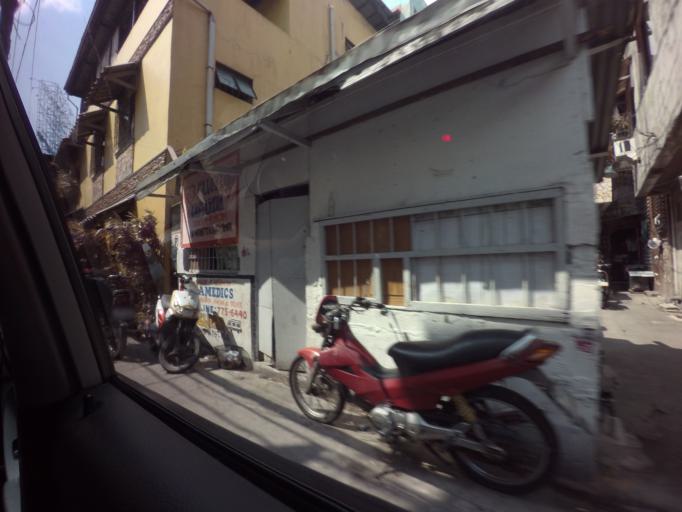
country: PH
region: Metro Manila
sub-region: San Juan
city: San Juan
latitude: 14.6012
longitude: 121.0107
